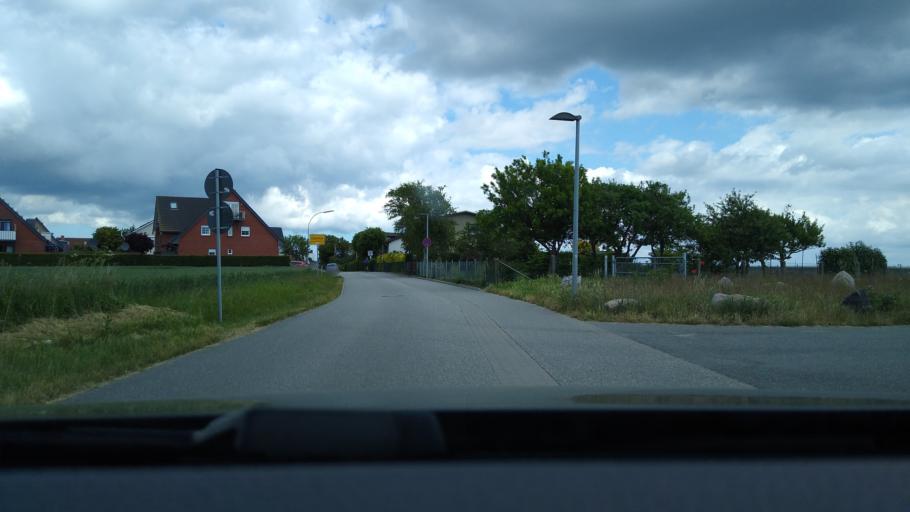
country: DE
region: Schleswig-Holstein
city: Dahme
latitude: 54.2155
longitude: 11.0895
